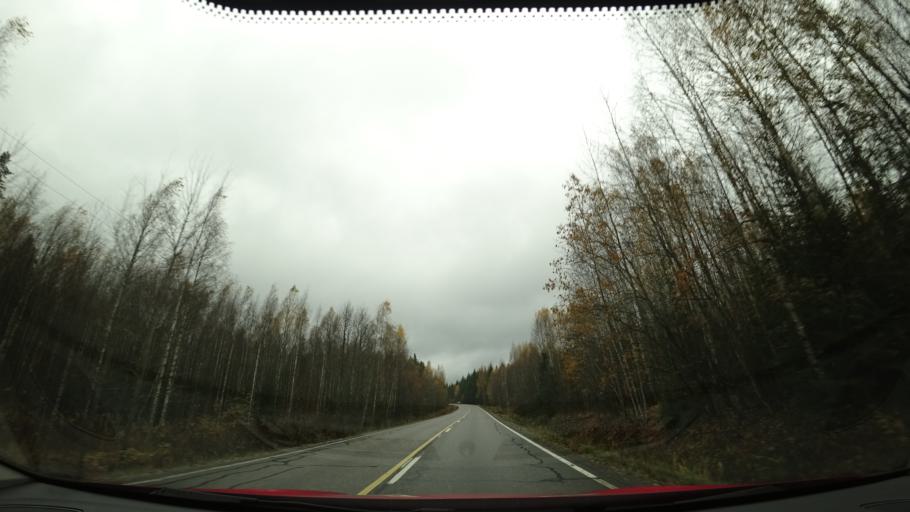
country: FI
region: Uusimaa
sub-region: Helsinki
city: Sibbo
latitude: 60.2822
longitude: 25.1962
